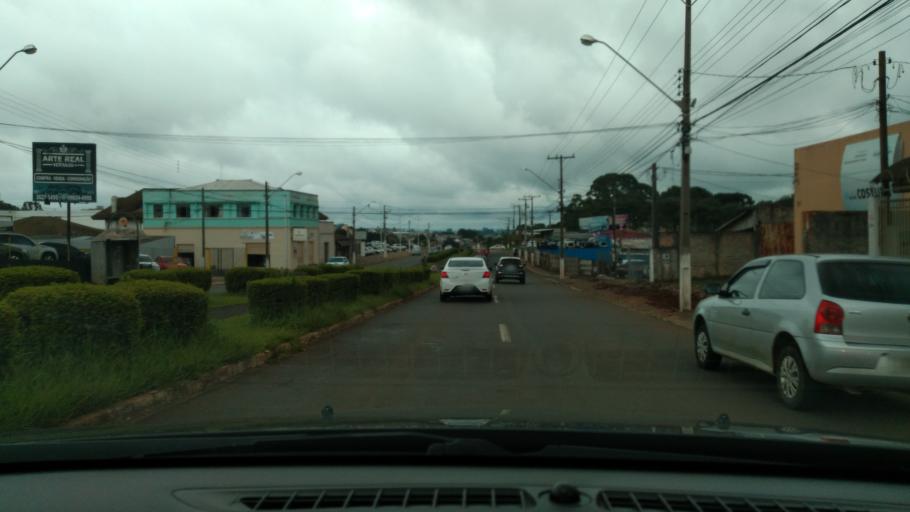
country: BR
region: Parana
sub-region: Guarapuava
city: Guarapuava
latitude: -25.3917
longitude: -51.4793
